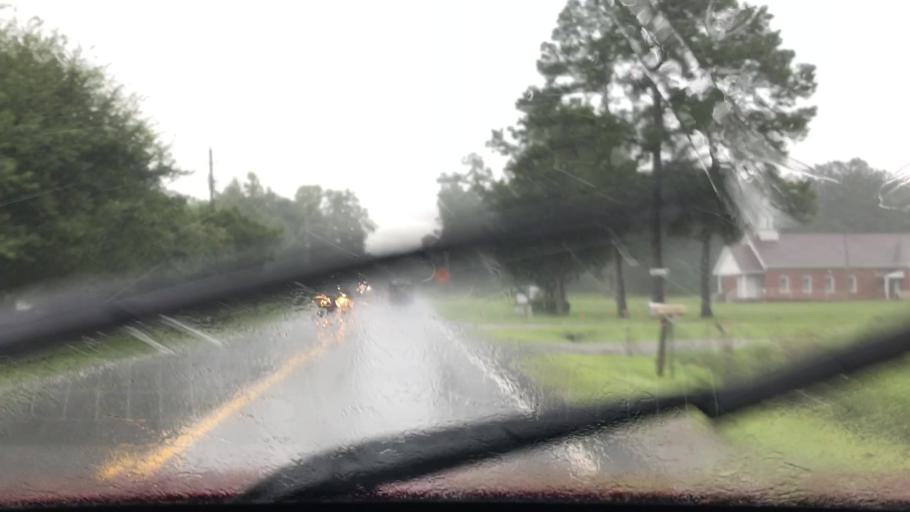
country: US
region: South Carolina
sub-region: Horry County
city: Loris
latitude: 33.9013
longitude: -78.8812
